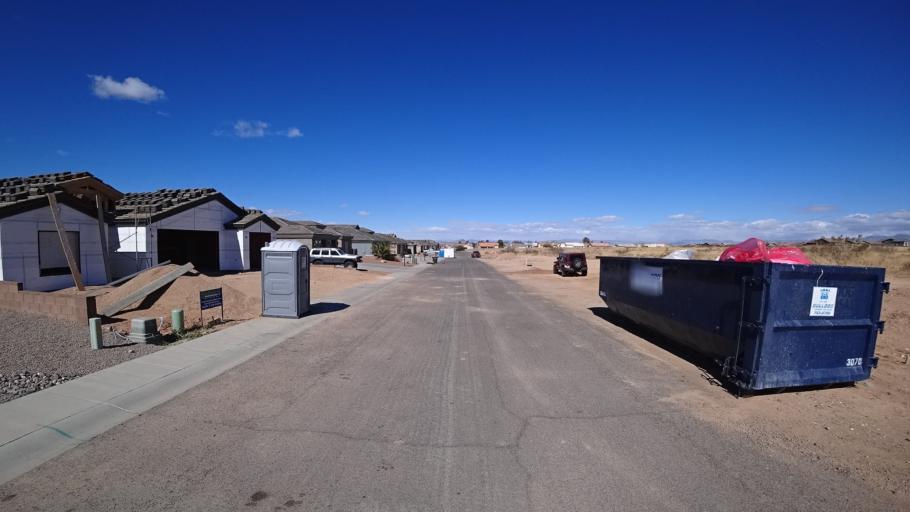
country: US
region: Arizona
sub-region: Mohave County
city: Kingman
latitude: 35.1896
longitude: -114.0050
